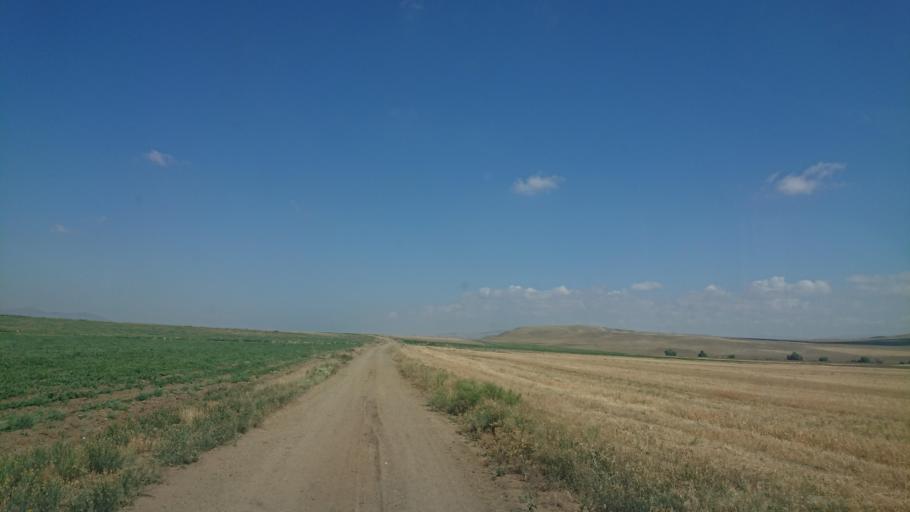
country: TR
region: Aksaray
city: Sariyahsi
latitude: 38.9642
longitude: 33.9259
